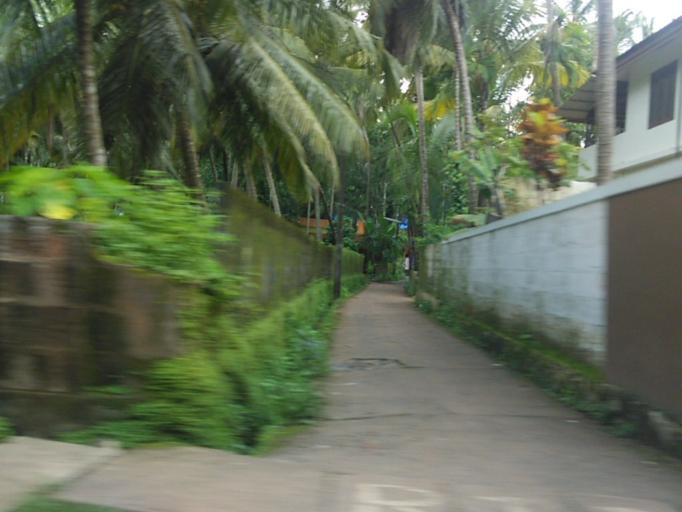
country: IN
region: Kerala
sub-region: Kozhikode
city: Kozhikode
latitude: 11.2842
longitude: 75.8111
